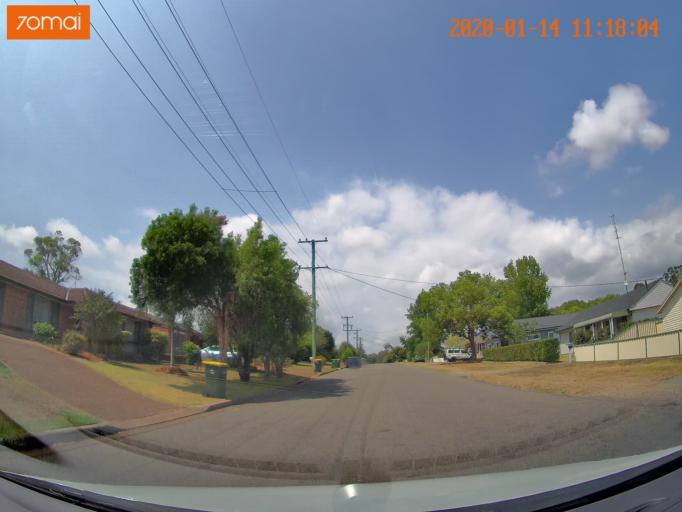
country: AU
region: New South Wales
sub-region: Lake Macquarie Shire
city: Cooranbong
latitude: -33.0950
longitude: 151.4609
